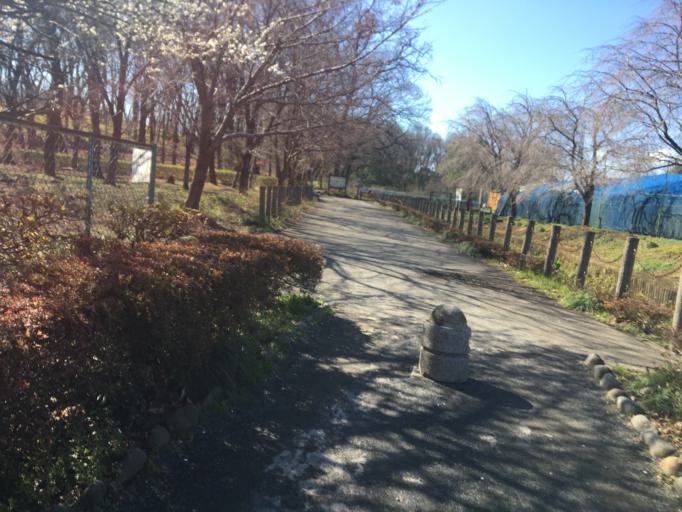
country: JP
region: Saitama
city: Asaka
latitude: 35.7950
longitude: 139.5582
